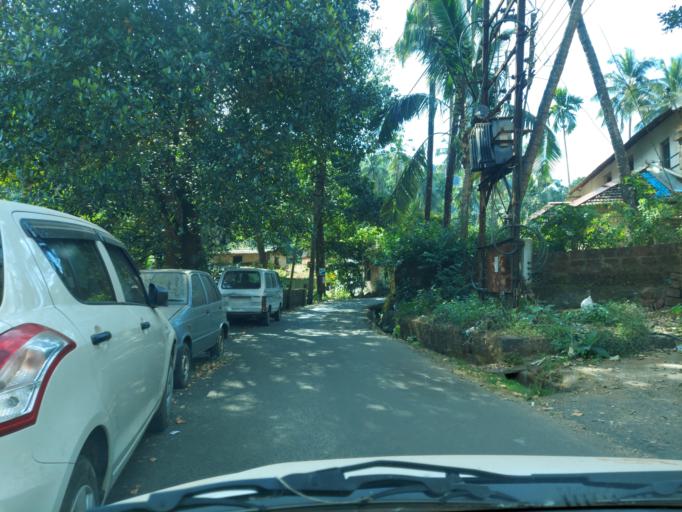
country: IN
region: Maharashtra
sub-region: Sindhudurg
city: Savantvadi
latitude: 15.9039
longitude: 73.8176
